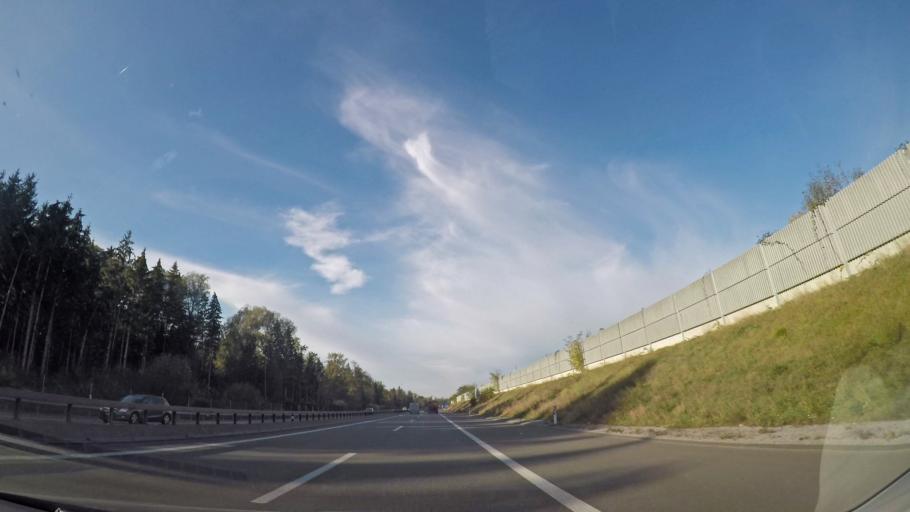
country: CH
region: Bern
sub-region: Bern-Mittelland District
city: Munsingen
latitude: 46.8708
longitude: 7.5463
